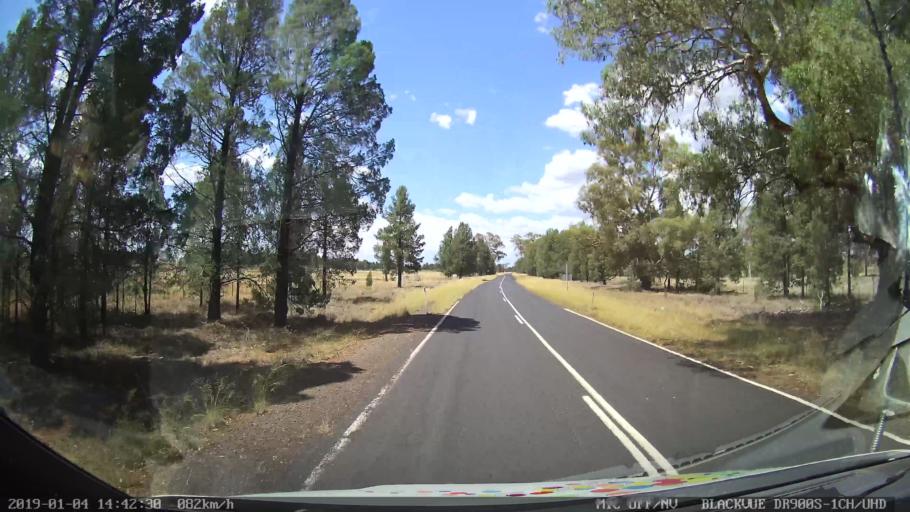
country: AU
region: New South Wales
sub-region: Dubbo Municipality
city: Dubbo
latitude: -32.1275
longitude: 148.6424
